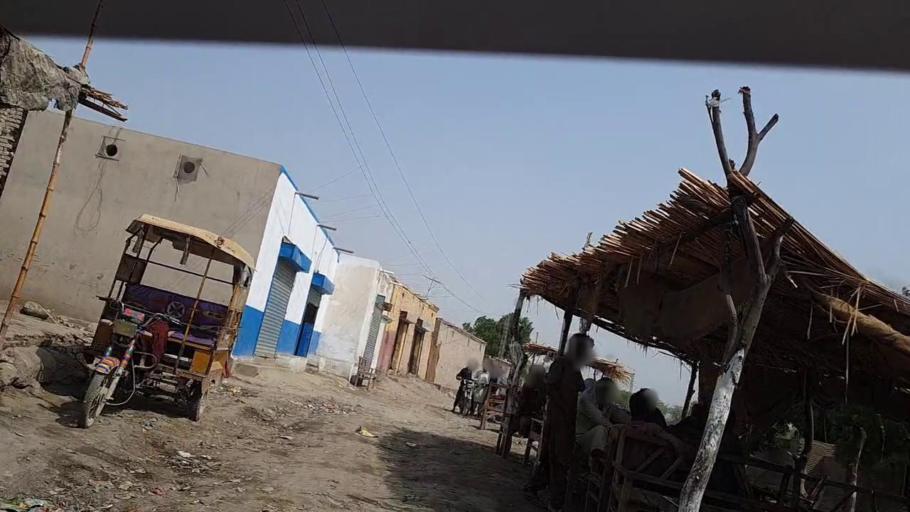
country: PK
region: Sindh
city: Khairpur Nathan Shah
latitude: 27.0770
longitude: 67.6881
